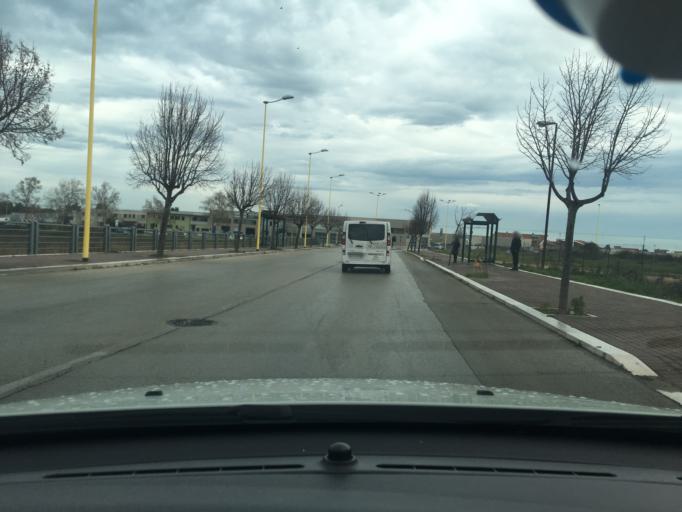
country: IT
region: Molise
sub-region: Provincia di Campobasso
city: Termoli
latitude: 41.9817
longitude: 14.9999
